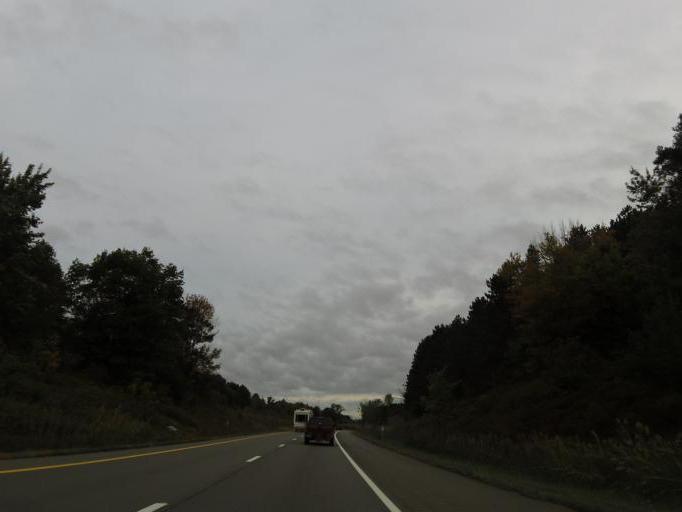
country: US
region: New York
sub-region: Erie County
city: Elma Center
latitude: 42.8170
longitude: -78.6594
